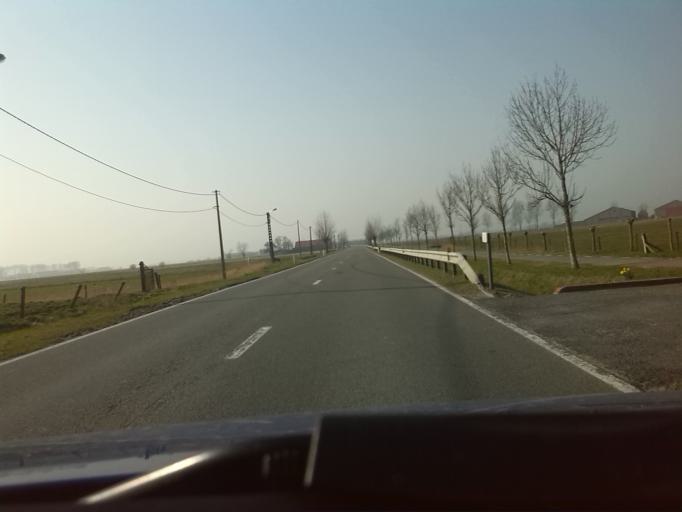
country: BE
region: Flanders
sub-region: Provincie West-Vlaanderen
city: Zuienkerke
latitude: 51.2538
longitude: 3.1226
